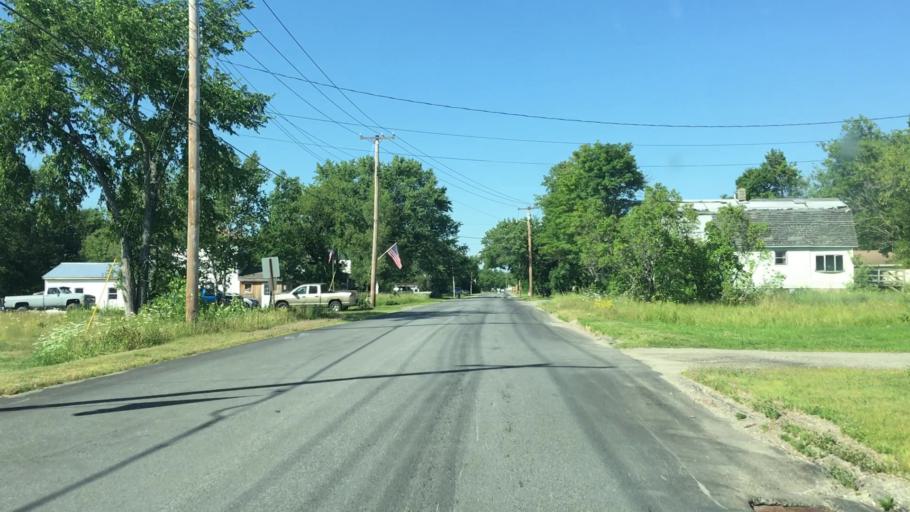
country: US
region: Maine
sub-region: Penobscot County
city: Howland
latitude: 45.2402
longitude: -68.6494
